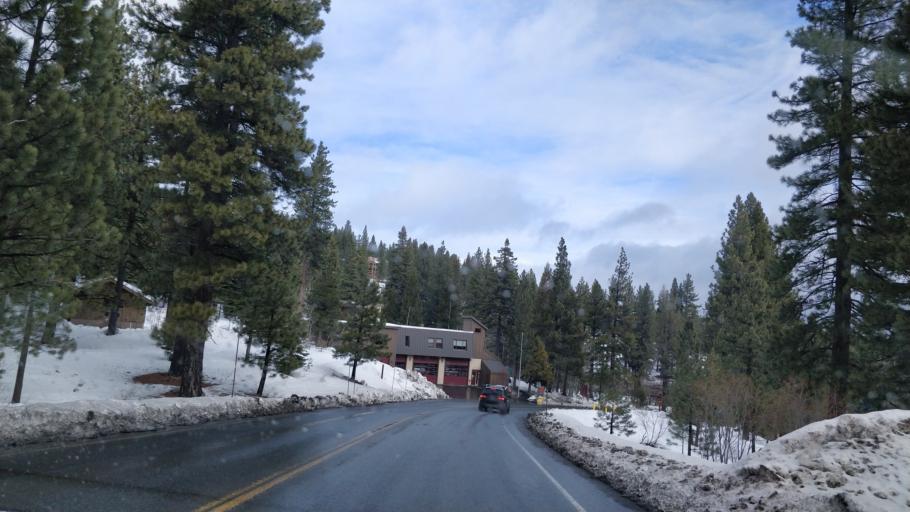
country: US
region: California
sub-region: Nevada County
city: Truckee
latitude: 39.2799
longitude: -120.1198
